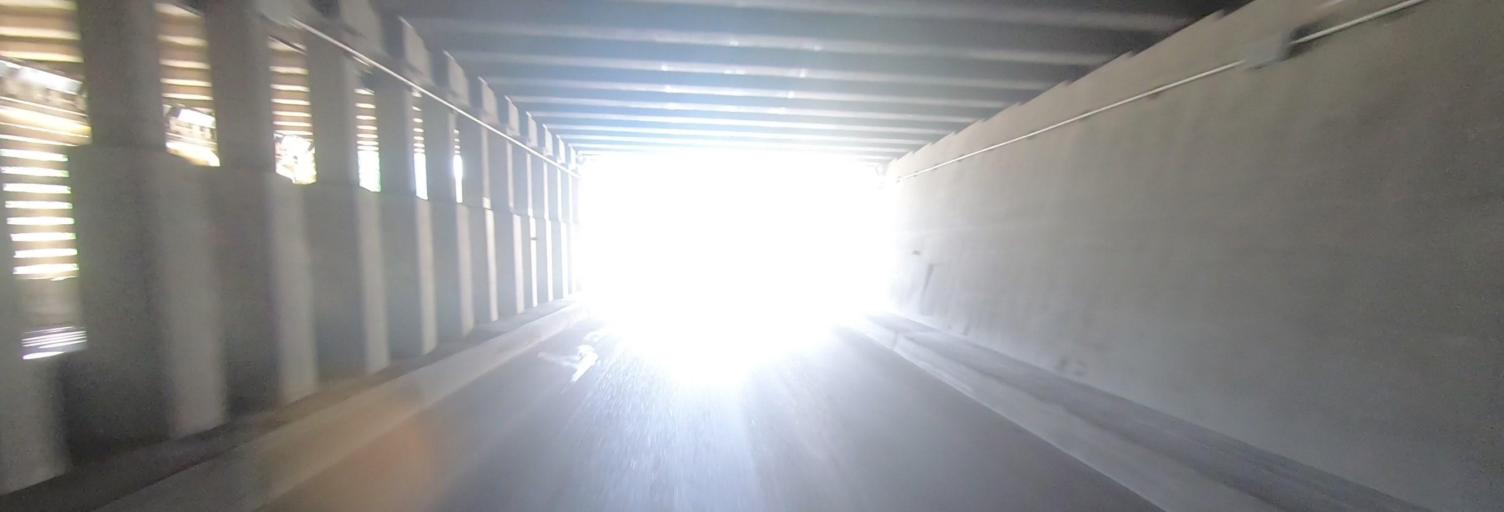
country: CA
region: British Columbia
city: Golden
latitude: 51.3300
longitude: -117.4636
